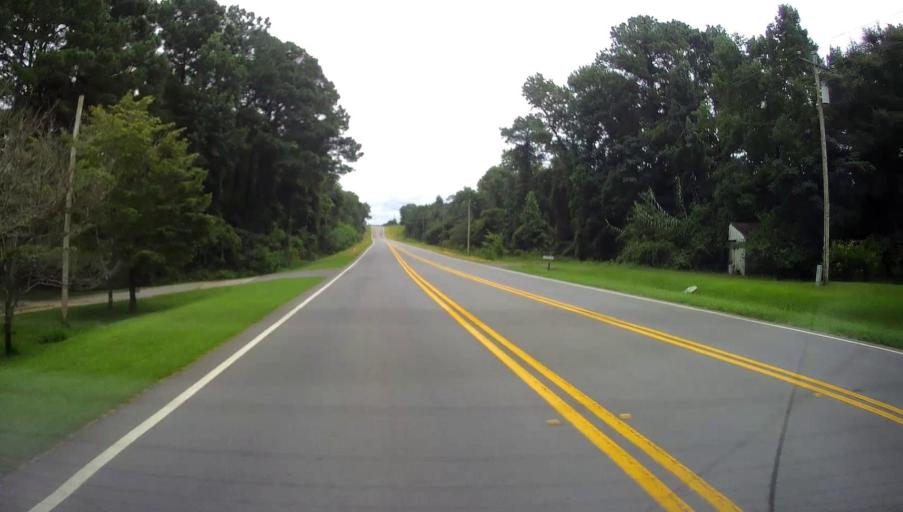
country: US
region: Georgia
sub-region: Macon County
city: Montezuma
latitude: 32.2929
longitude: -83.9444
